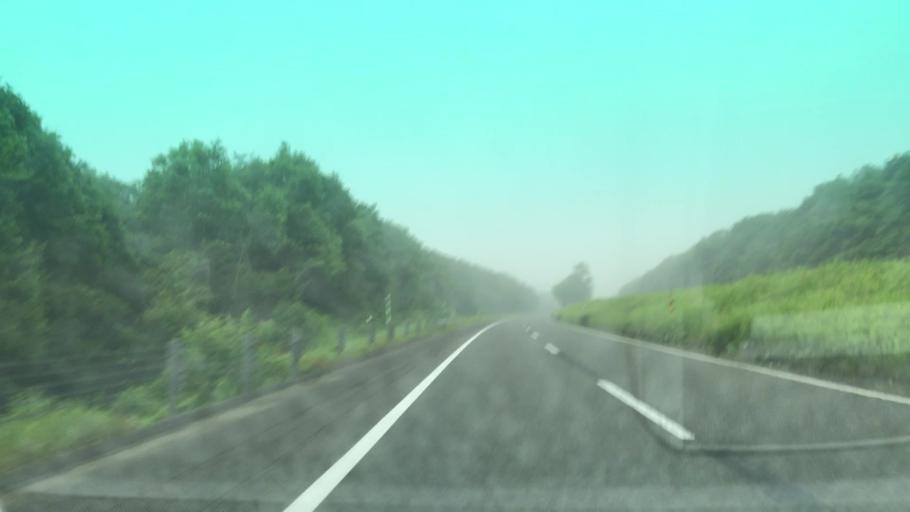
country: JP
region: Hokkaido
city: Chitose
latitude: 42.7946
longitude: 141.6270
